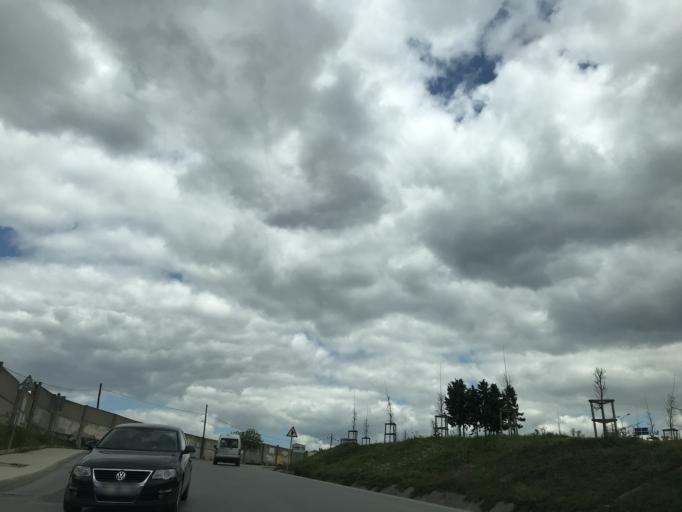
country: TR
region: Istanbul
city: Maltepe
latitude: 40.9017
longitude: 29.2073
